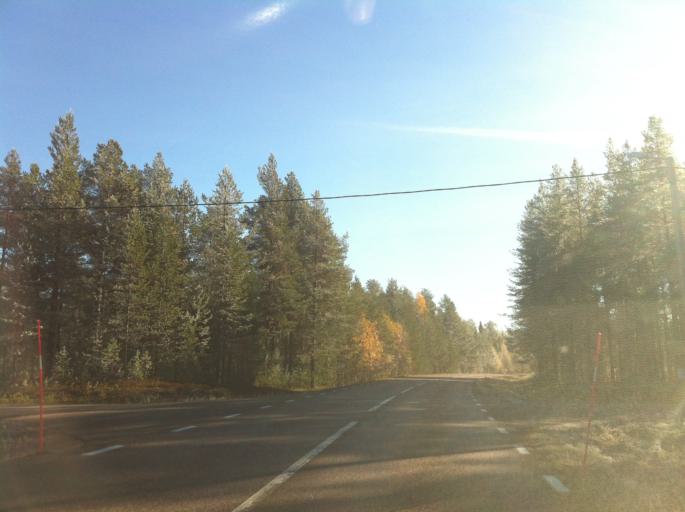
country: NO
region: Hedmark
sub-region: Trysil
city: Innbygda
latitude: 61.7471
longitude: 12.9701
